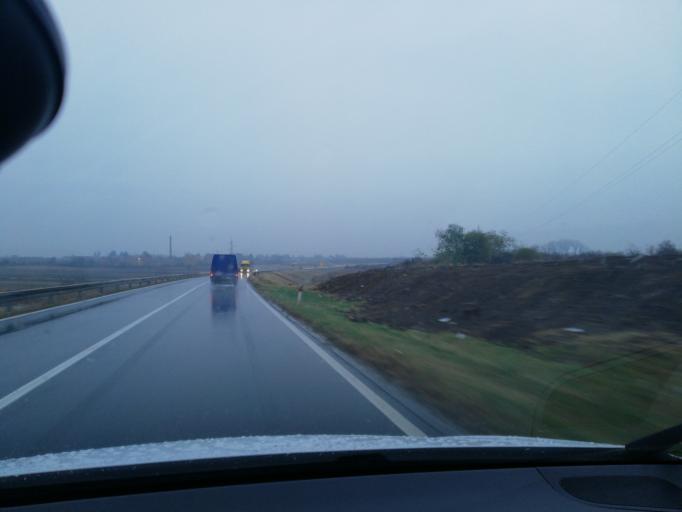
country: RS
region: Autonomna Pokrajina Vojvodina
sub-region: Sremski Okrug
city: Ruma
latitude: 45.0146
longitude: 19.8447
